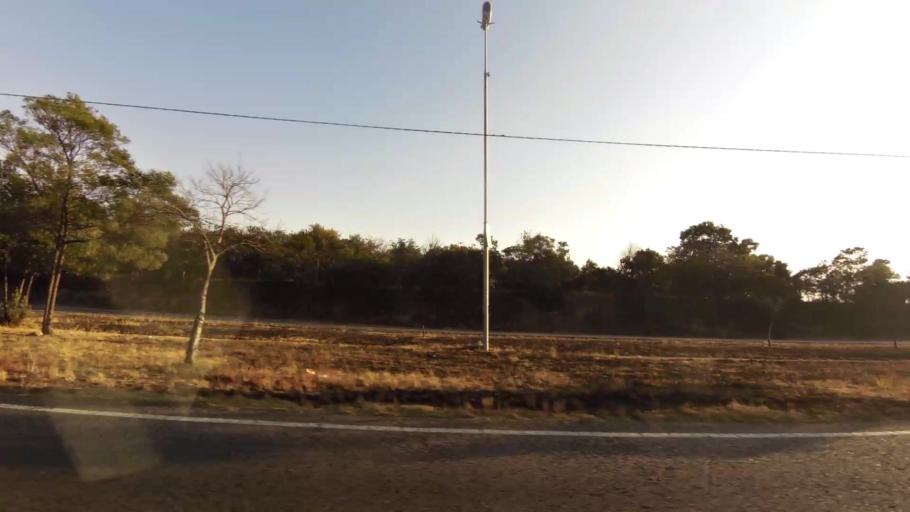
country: ZA
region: Gauteng
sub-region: City of Johannesburg Metropolitan Municipality
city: Johannesburg
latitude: -26.2684
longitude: 27.9691
